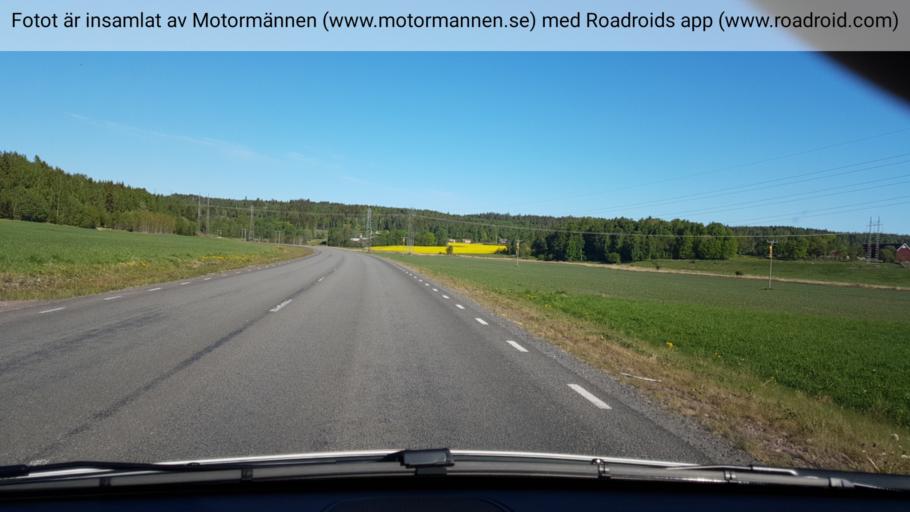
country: SE
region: Vaestra Goetaland
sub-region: Skovde Kommun
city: Stopen
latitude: 58.5349
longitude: 13.7589
